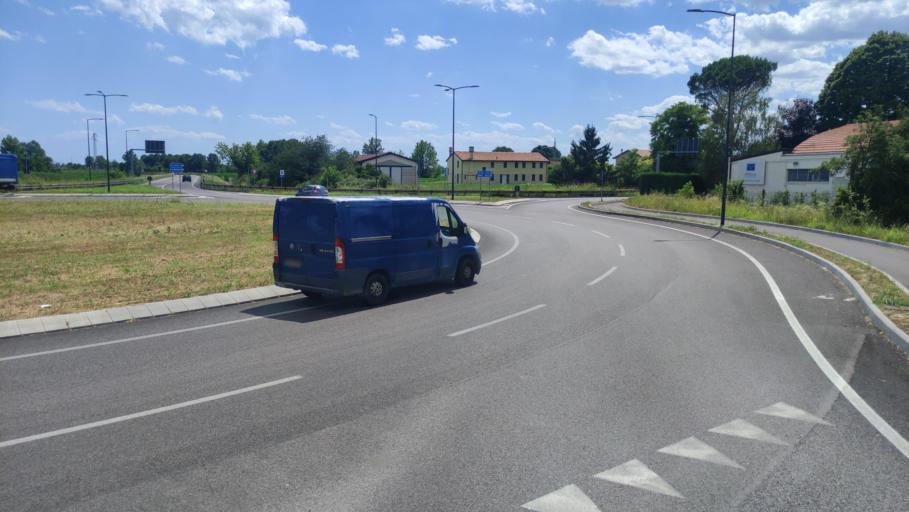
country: IT
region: Veneto
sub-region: Provincia di Venezia
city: Scorze
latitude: 45.5677
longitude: 12.1022
